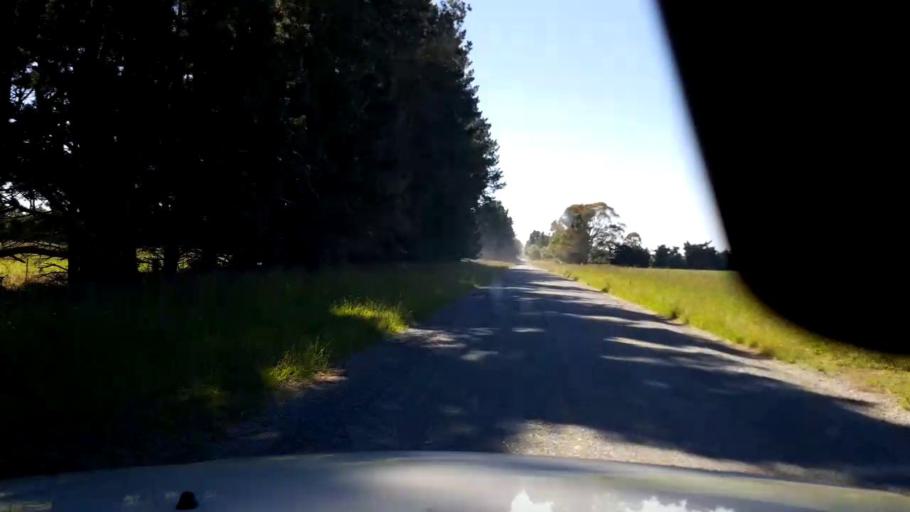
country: NZ
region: Canterbury
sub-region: Timaru District
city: Pleasant Point
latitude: -43.9747
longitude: 171.2585
